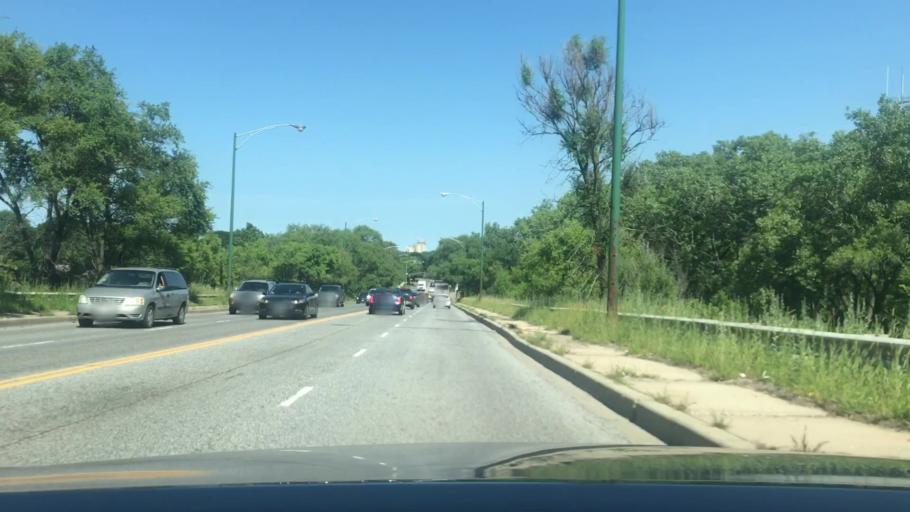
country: US
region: Illinois
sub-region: Cook County
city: Burnham
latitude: 41.7080
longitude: -87.5716
